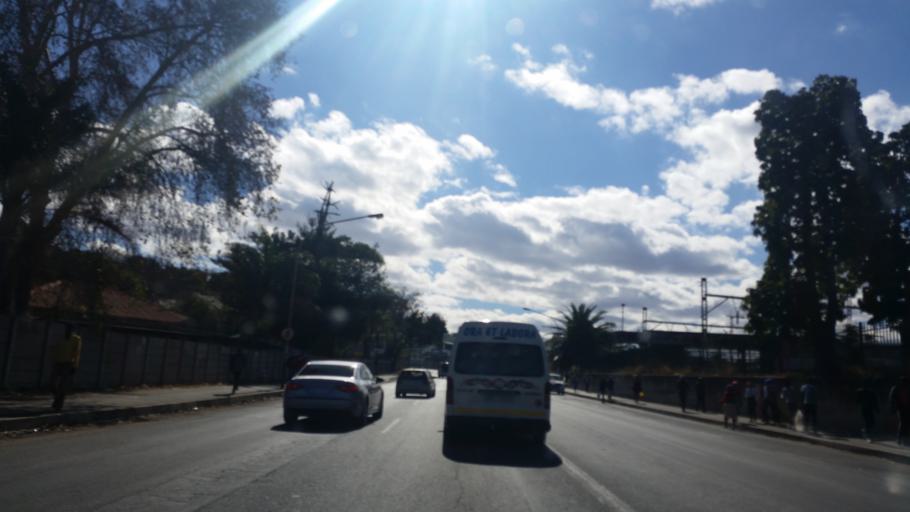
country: ZA
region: KwaZulu-Natal
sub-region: uThukela District Municipality
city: Ladysmith
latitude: -28.5570
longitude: 29.7852
